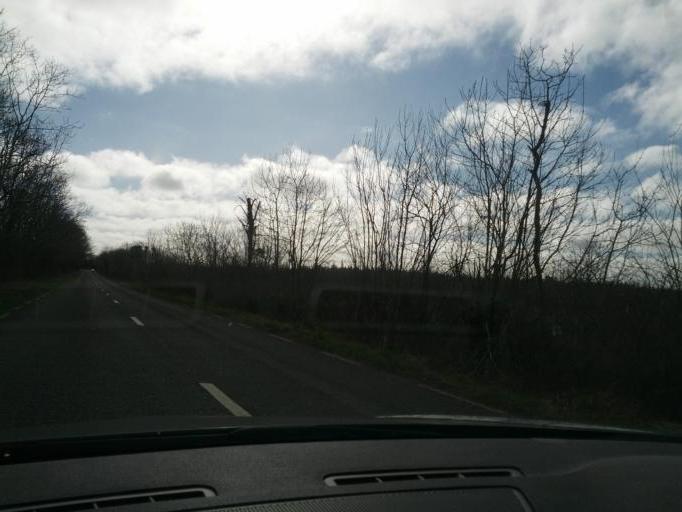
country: IE
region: Connaught
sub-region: County Galway
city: Ballinasloe
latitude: 53.4211
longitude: -8.3917
